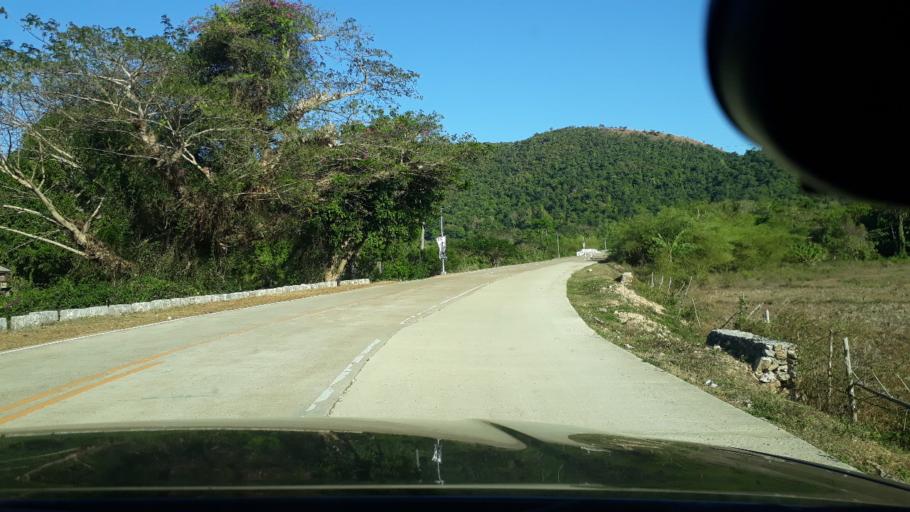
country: PH
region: Mimaropa
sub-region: Province of Palawan
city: Coron
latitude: 12.0489
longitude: 120.1525
